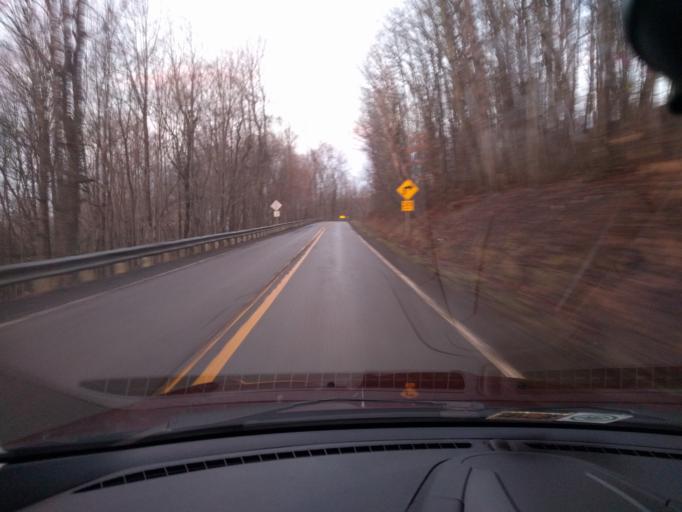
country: US
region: West Virginia
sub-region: Greenbrier County
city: Rainelle
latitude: 37.9981
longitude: -80.8745
